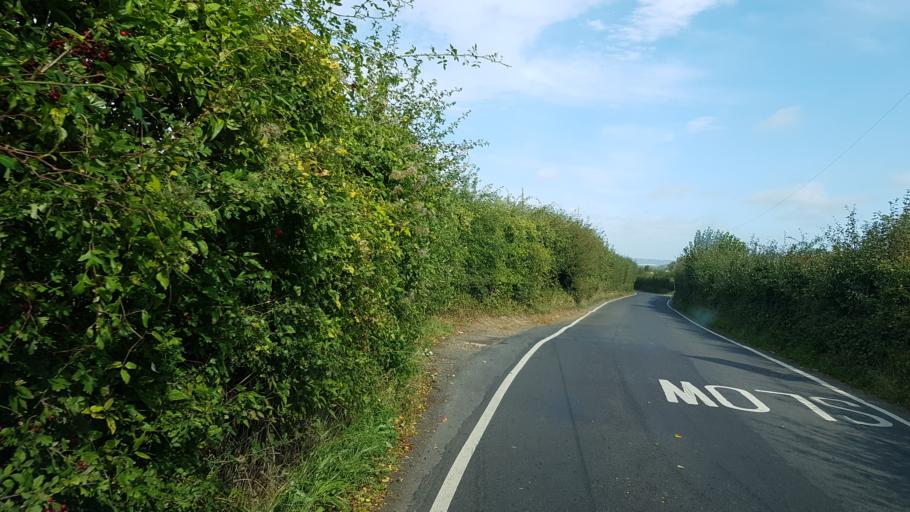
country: GB
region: England
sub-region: Kent
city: Yalding
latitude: 51.2426
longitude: 0.4660
